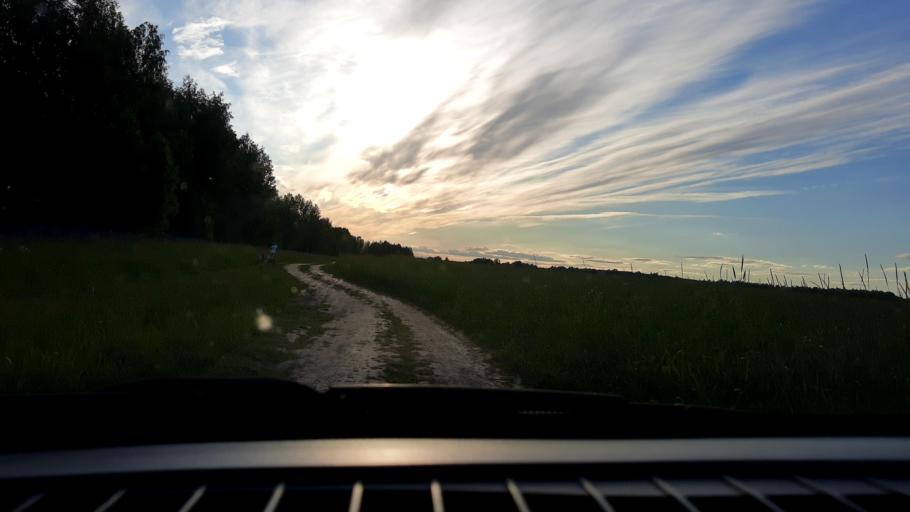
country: RU
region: Nizjnij Novgorod
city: Kstovo
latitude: 56.2632
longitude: 44.3175
